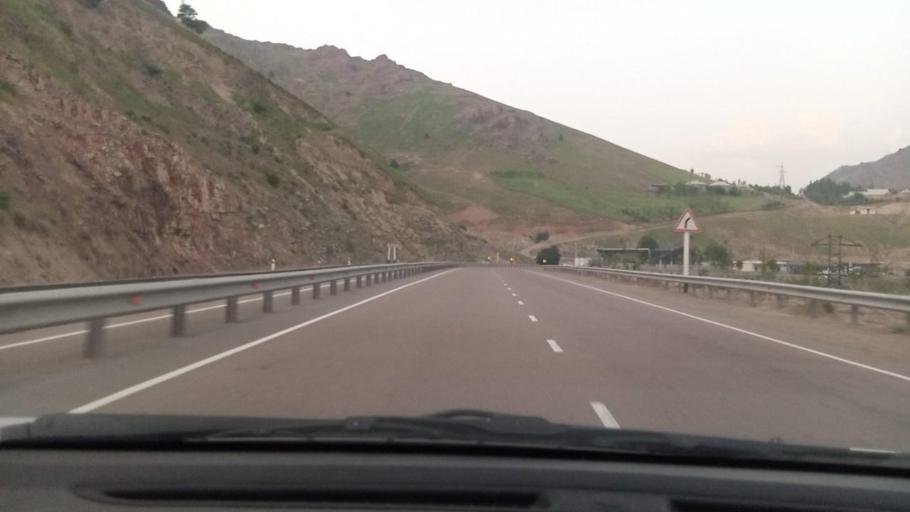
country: UZ
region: Toshkent
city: Angren
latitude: 41.1255
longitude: 70.3565
